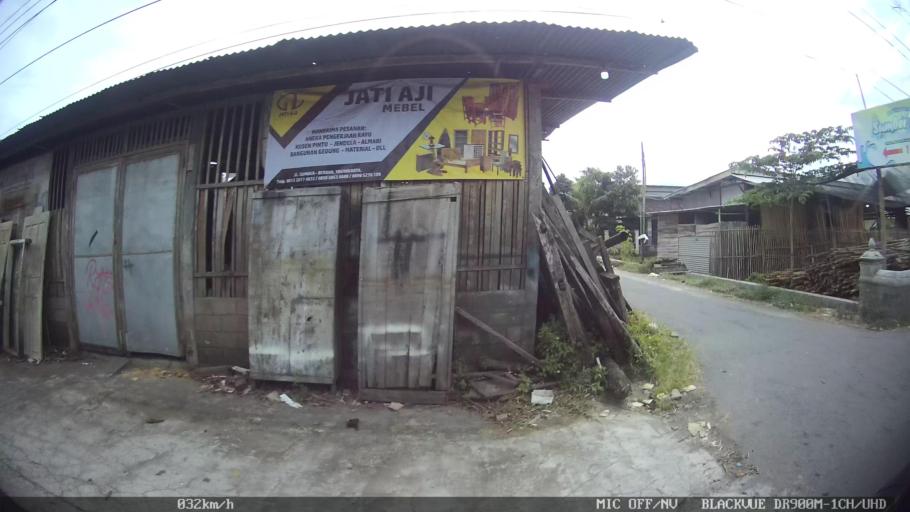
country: ID
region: Daerah Istimewa Yogyakarta
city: Depok
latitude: -7.8049
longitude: 110.4482
